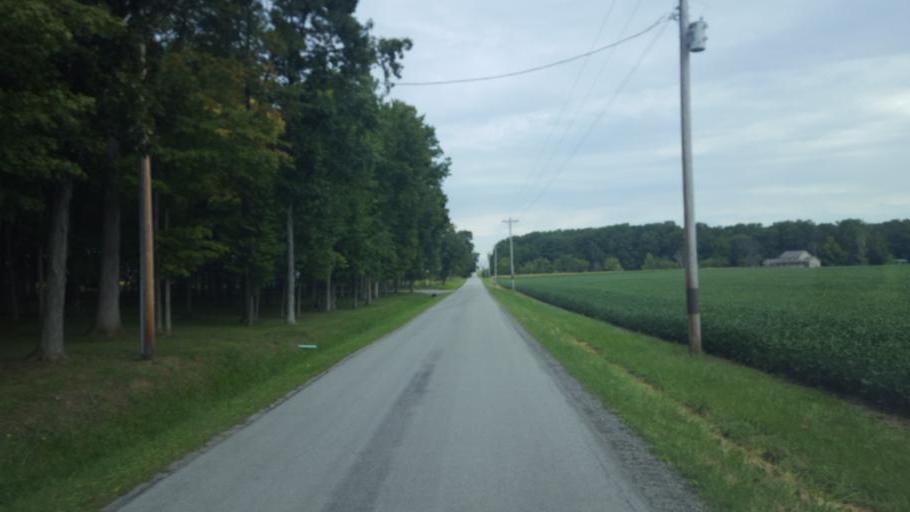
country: US
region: Ohio
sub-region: Wyandot County
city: Upper Sandusky
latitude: 40.7773
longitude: -83.1884
